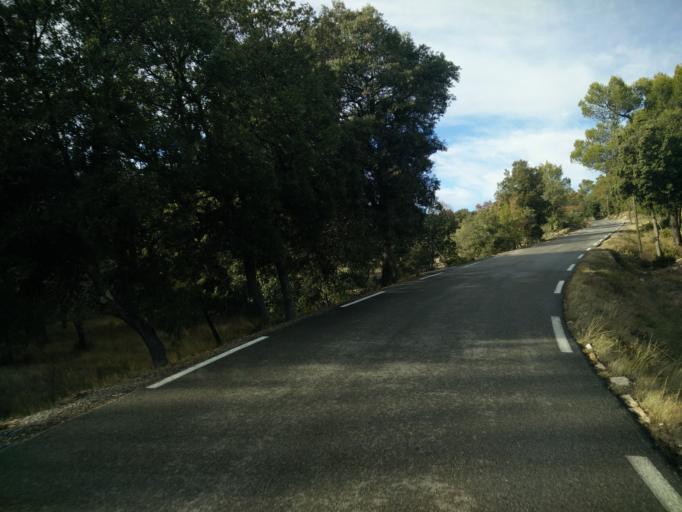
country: FR
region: Provence-Alpes-Cote d'Azur
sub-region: Departement du Var
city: Cotignac
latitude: 43.5450
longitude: 6.1318
